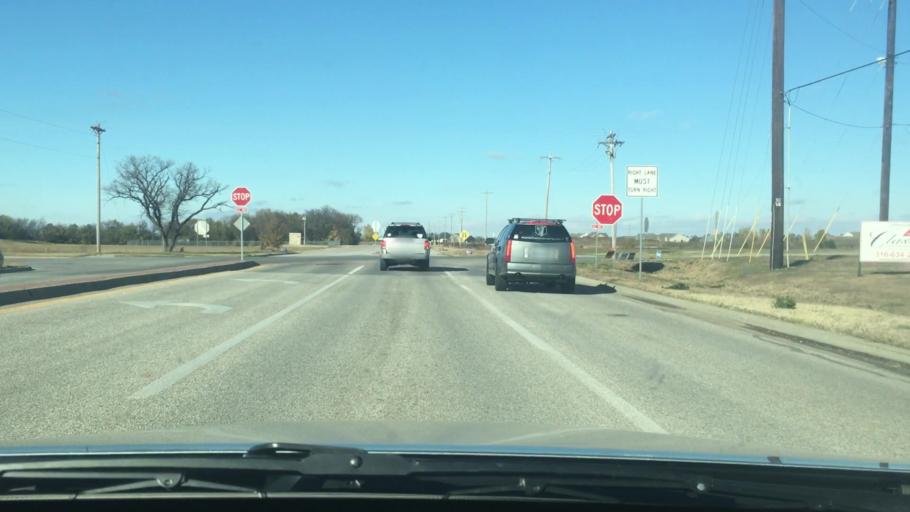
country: US
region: Kansas
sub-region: Sedgwick County
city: Maize
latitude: 37.7364
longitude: -97.4809
